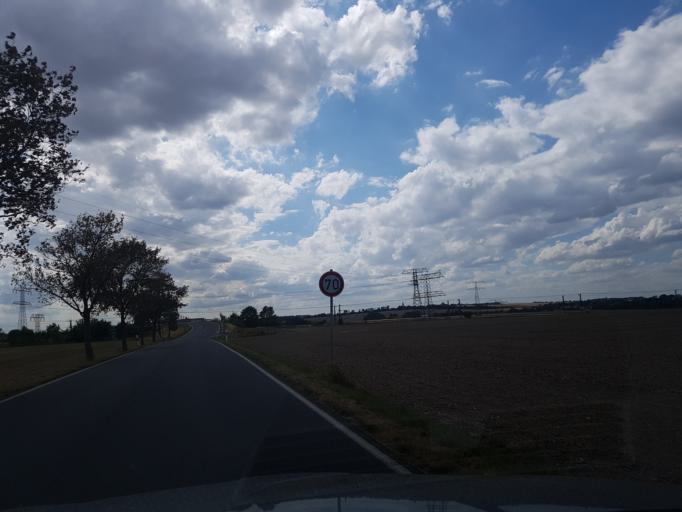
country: DE
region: Saxony
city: Priestewitz
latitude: 51.2393
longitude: 13.5470
